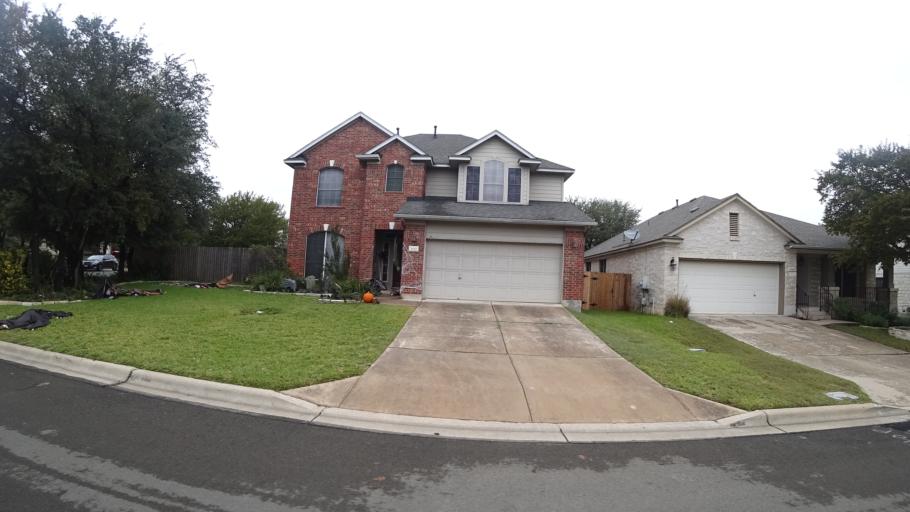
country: US
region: Texas
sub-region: Travis County
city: Shady Hollow
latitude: 30.1891
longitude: -97.8694
